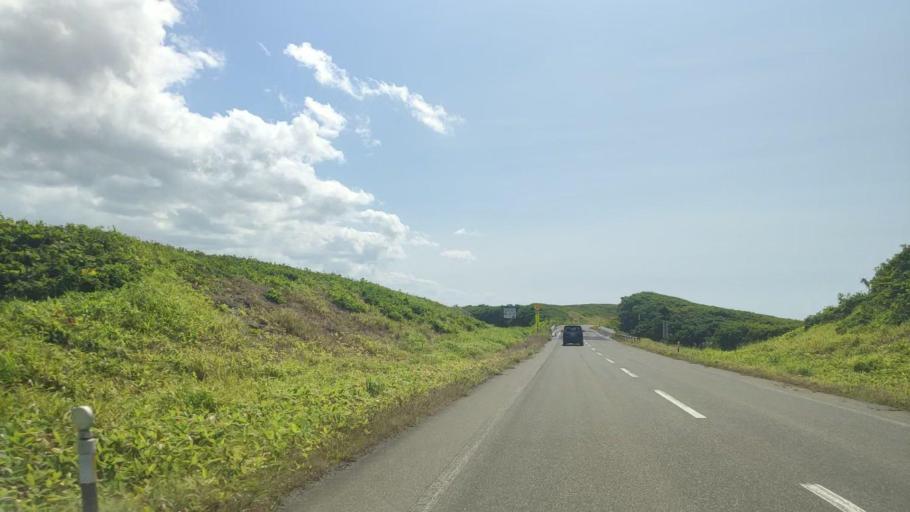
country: JP
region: Hokkaido
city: Wakkanai
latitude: 45.1953
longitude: 141.5740
